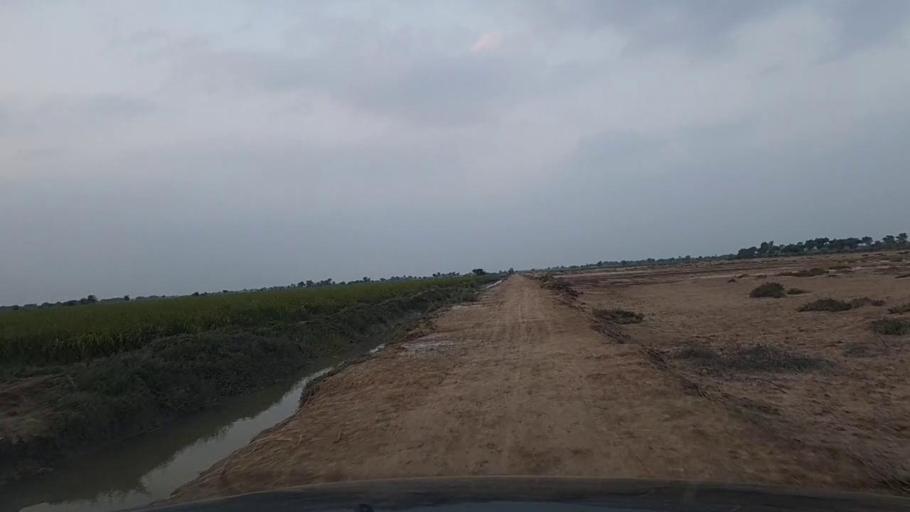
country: PK
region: Sindh
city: Jati
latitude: 24.5004
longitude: 68.3931
